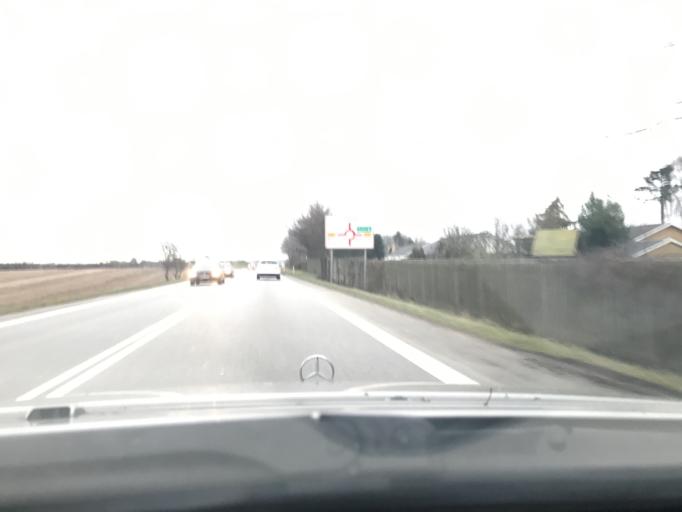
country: DK
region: South Denmark
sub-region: Aabenraa Kommune
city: Rodekro
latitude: 55.0745
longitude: 9.3373
